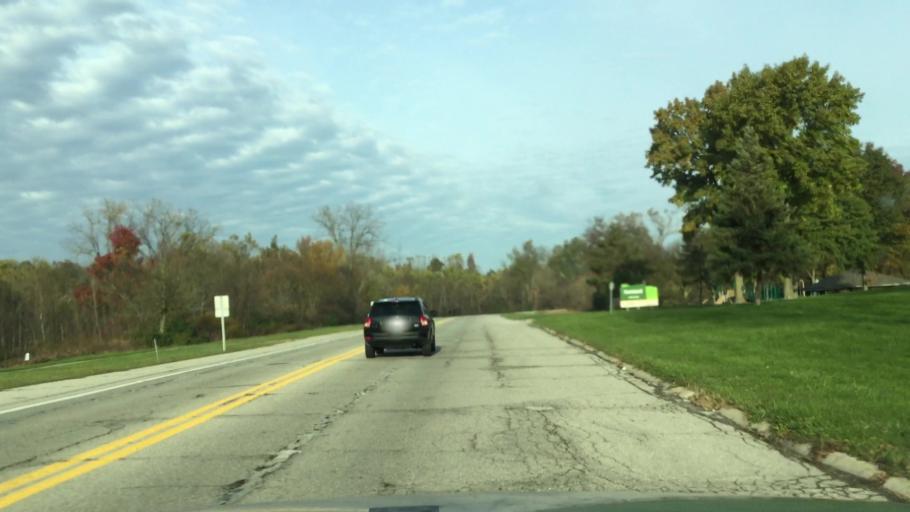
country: US
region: Michigan
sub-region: Wayne County
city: Dearborn Heights
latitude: 42.3324
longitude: -83.2544
